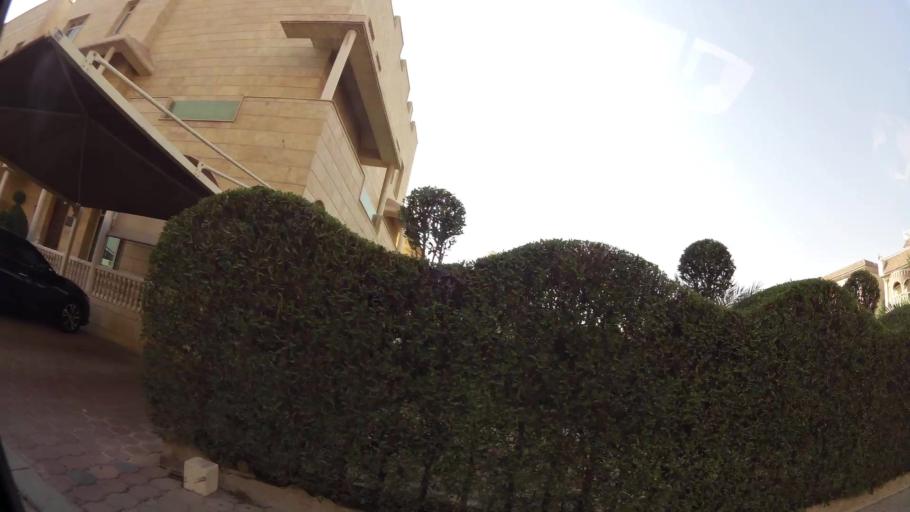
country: KW
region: Muhafazat al Jahra'
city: Al Jahra'
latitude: 29.3058
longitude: 47.7884
